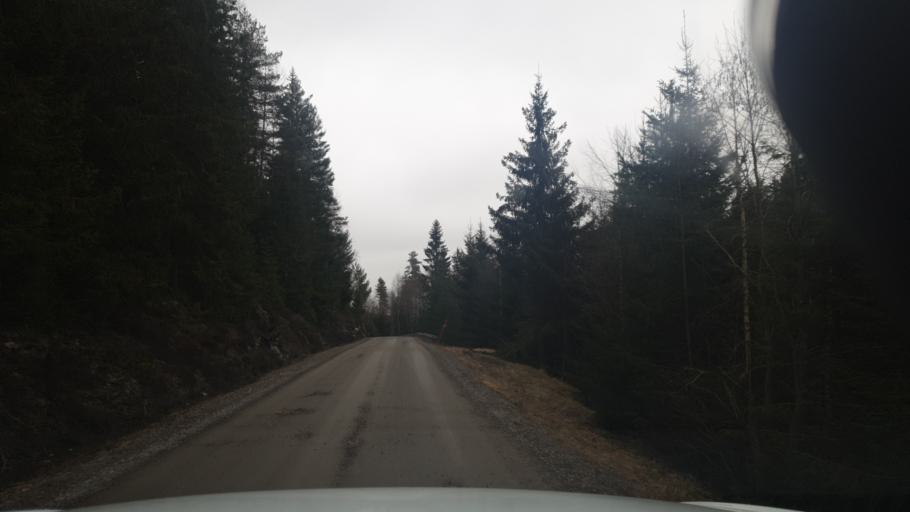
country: NO
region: Ostfold
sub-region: Romskog
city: Romskog
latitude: 59.7087
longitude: 12.0407
